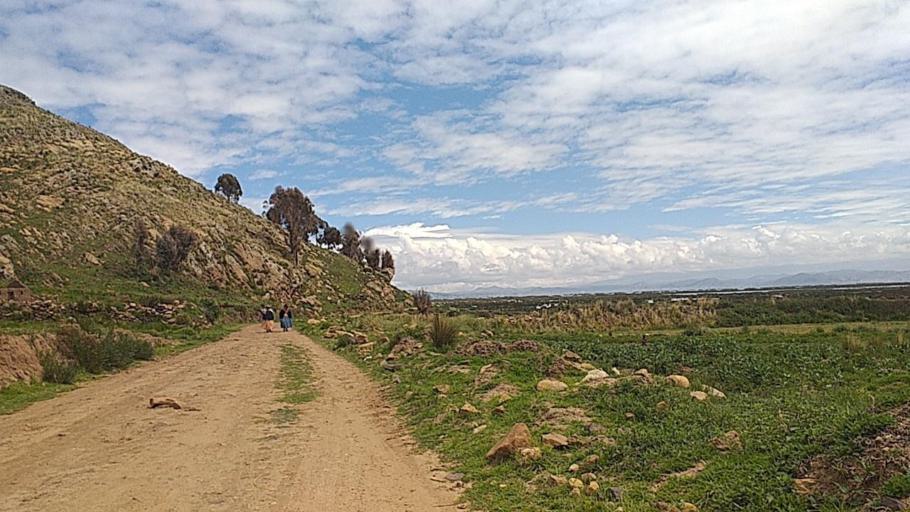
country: BO
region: La Paz
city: Batallas
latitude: -16.3361
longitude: -68.6378
